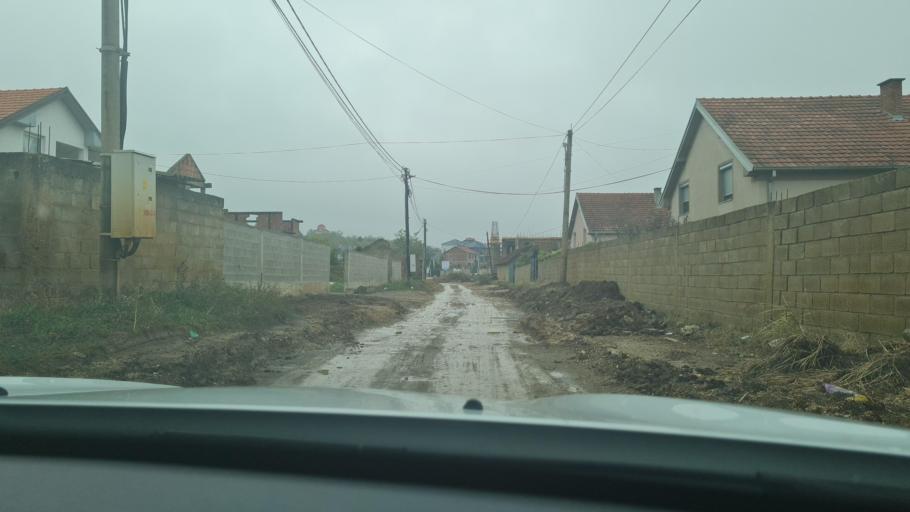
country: MK
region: Opstina Lipkovo
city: Matejche
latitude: 42.1197
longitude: 21.6039
